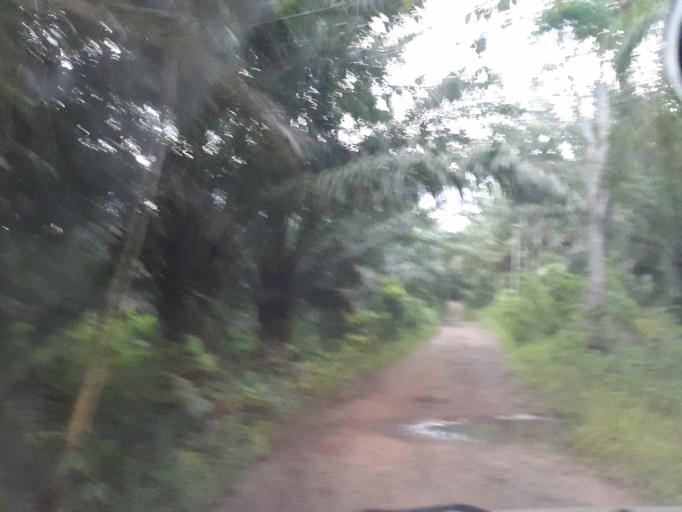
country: ID
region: Lampung
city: Sidorejo
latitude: -5.5546
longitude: 105.5238
